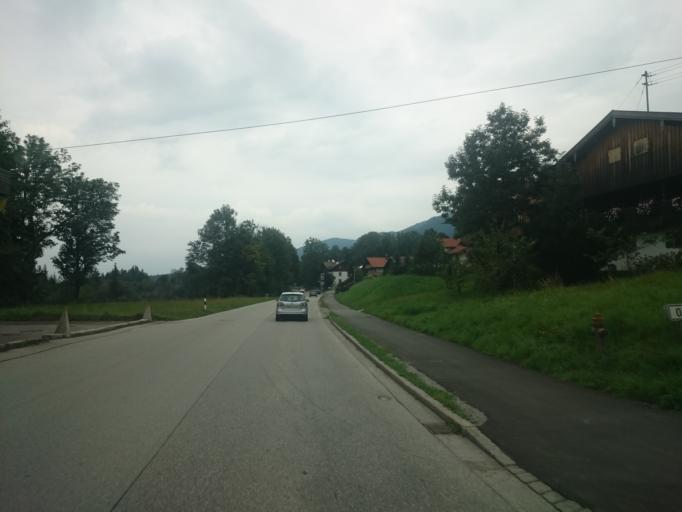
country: DE
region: Bavaria
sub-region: Upper Bavaria
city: Lenggries
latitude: 47.6529
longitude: 11.5887
